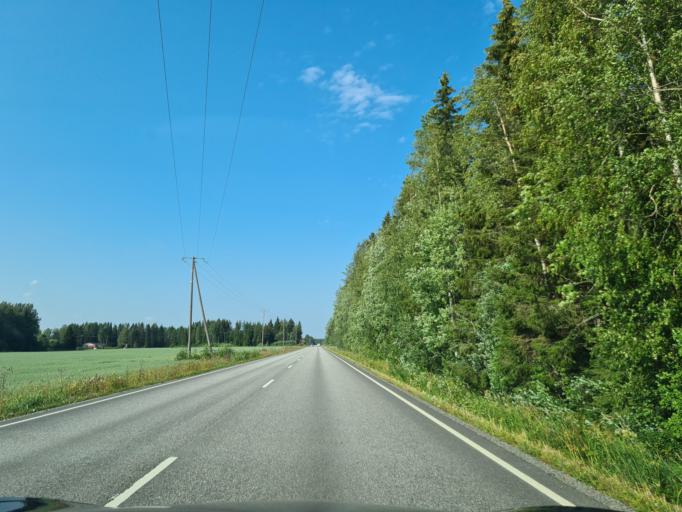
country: FI
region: Satakunta
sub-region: Pohjois-Satakunta
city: Kankaanpaeae
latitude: 61.9102
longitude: 22.5007
